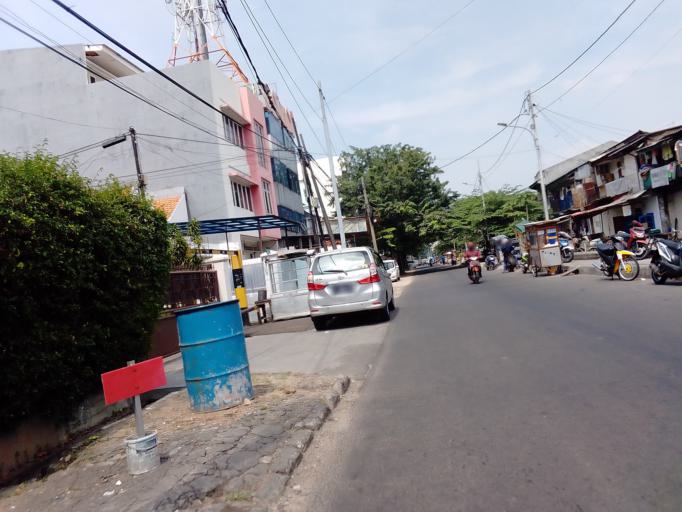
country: ID
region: Jakarta Raya
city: Jakarta
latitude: -6.1750
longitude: 106.8073
